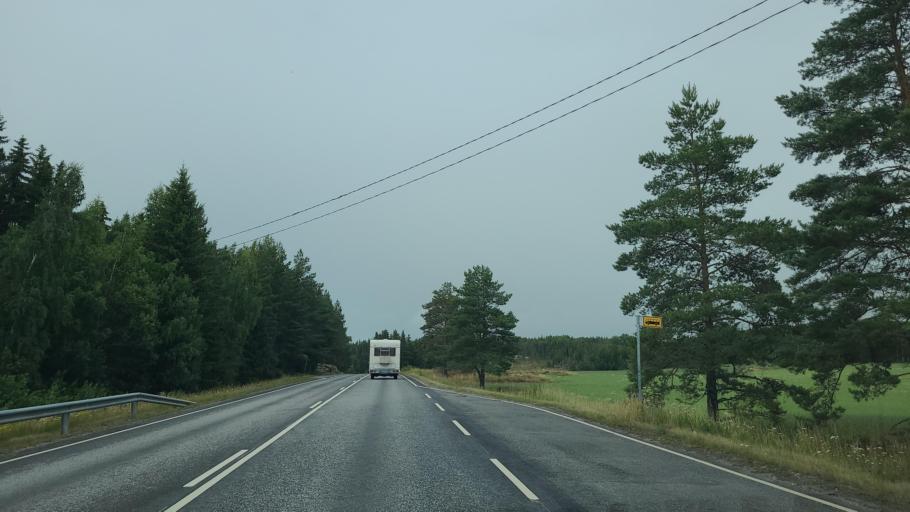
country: FI
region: Varsinais-Suomi
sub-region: Turku
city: Sauvo
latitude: 60.2955
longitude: 22.6766
